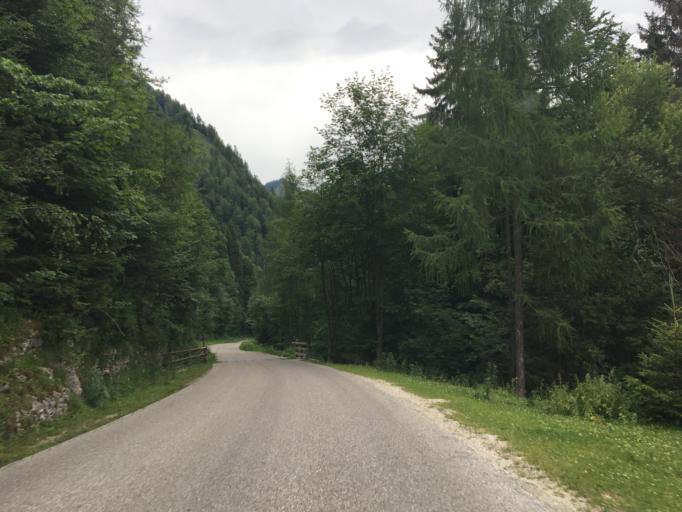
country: AT
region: Salzburg
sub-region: Politischer Bezirk Salzburg-Umgebung
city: Strobl
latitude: 47.6637
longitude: 13.4553
